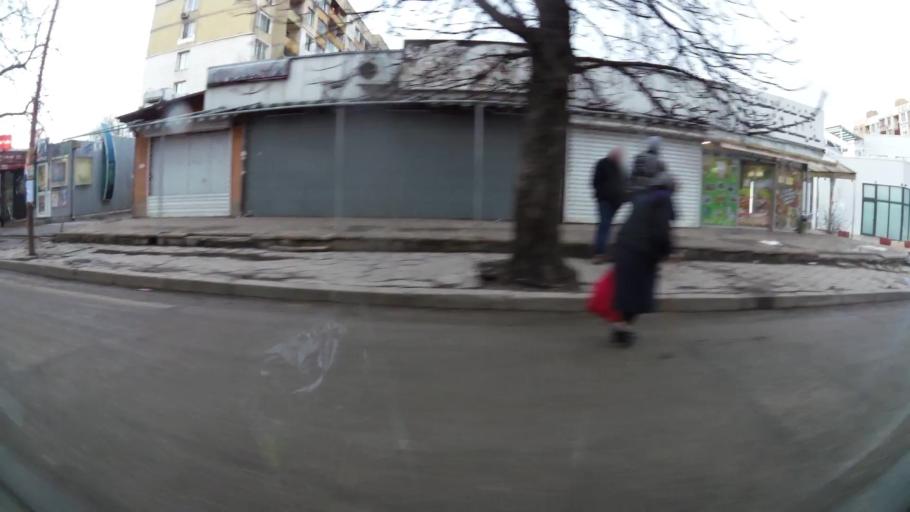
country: BG
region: Sofia-Capital
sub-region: Stolichna Obshtina
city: Sofia
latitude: 42.7334
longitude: 23.3029
